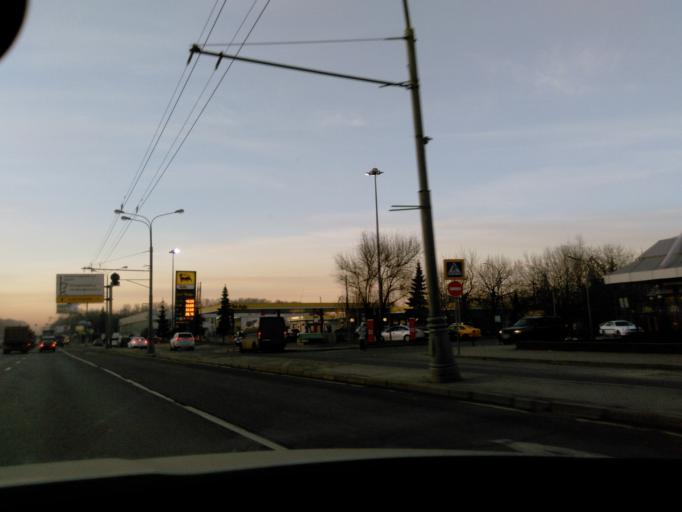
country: RU
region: Moskovskaya
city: Levoberezhnyy
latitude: 55.8659
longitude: 37.4627
